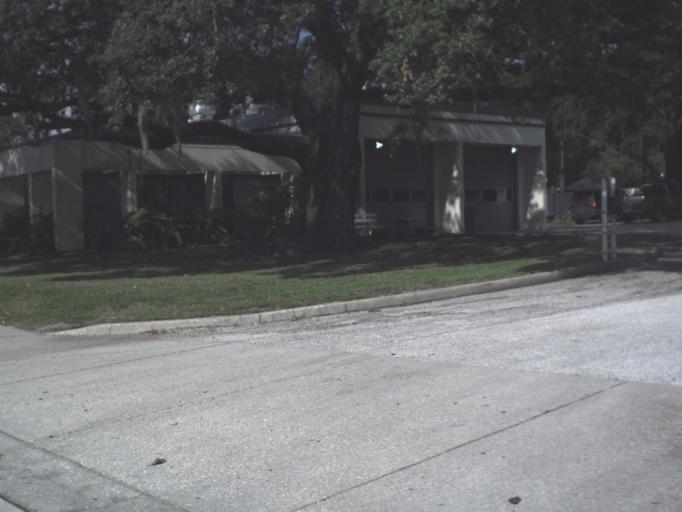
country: US
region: Florida
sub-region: Hillsborough County
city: Tampa
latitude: 28.0028
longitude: -82.4512
